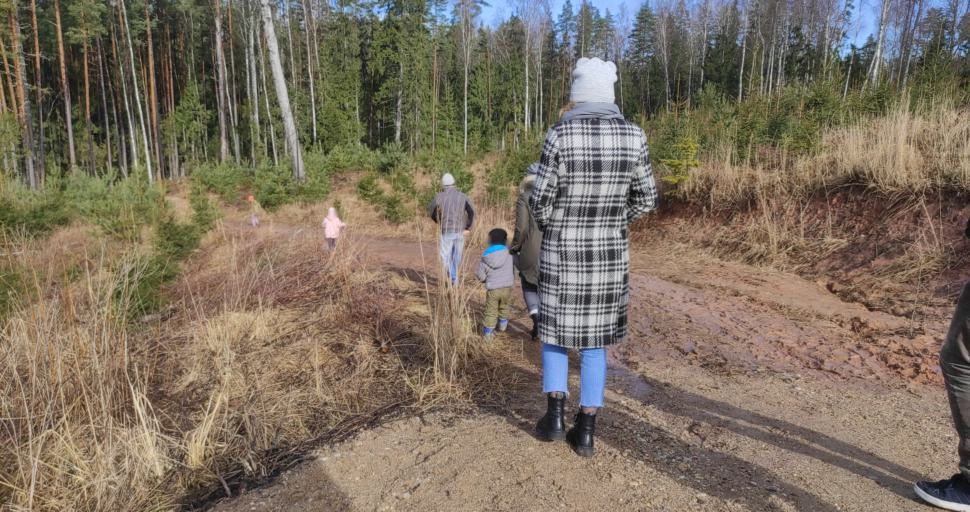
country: LV
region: Tukuma Rajons
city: Tukums
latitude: 57.1120
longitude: 23.0438
